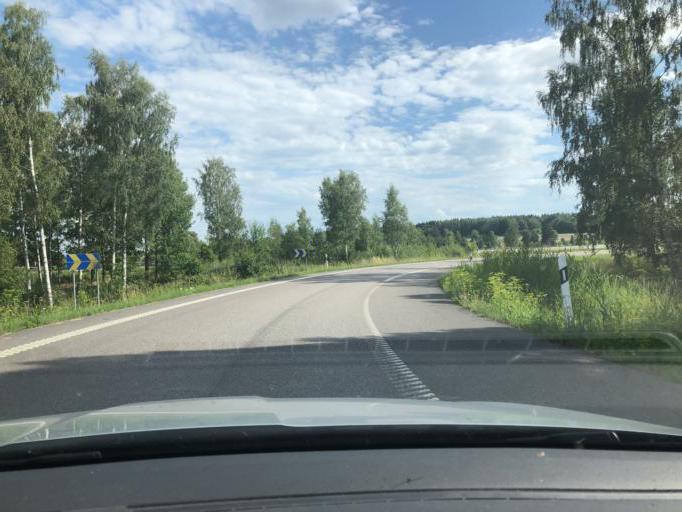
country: SE
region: OEstergoetland
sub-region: Mjolby Kommun
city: Mjolby
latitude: 58.3447
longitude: 15.1769
